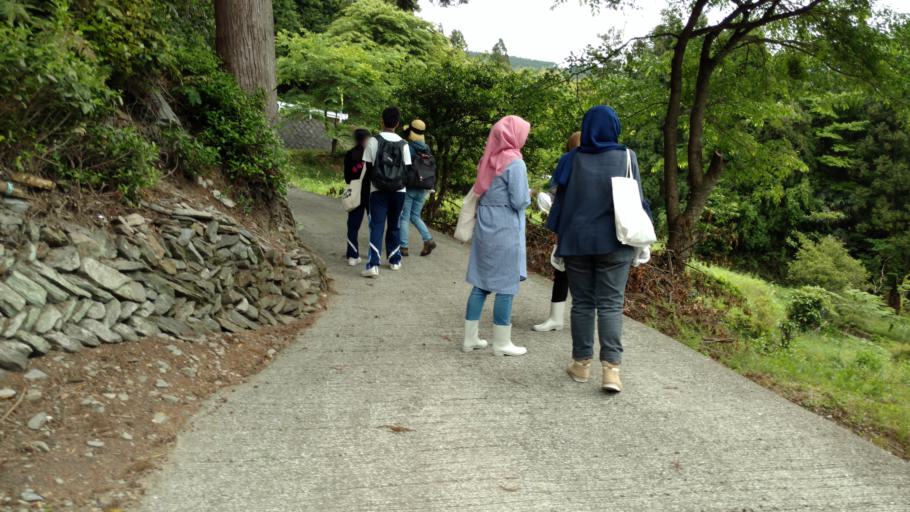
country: JP
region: Ehime
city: Saijo
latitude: 33.8667
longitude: 133.1986
